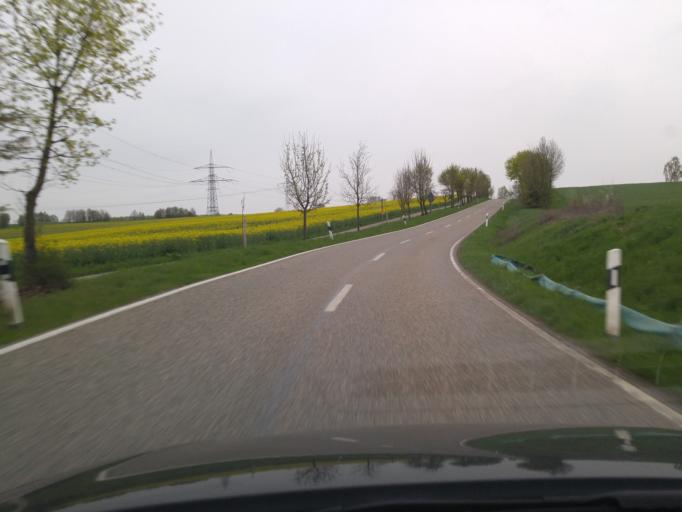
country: DE
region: Baden-Wuerttemberg
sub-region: Regierungsbezirk Stuttgart
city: Bad Rappenau
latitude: 49.2552
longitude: 9.1110
